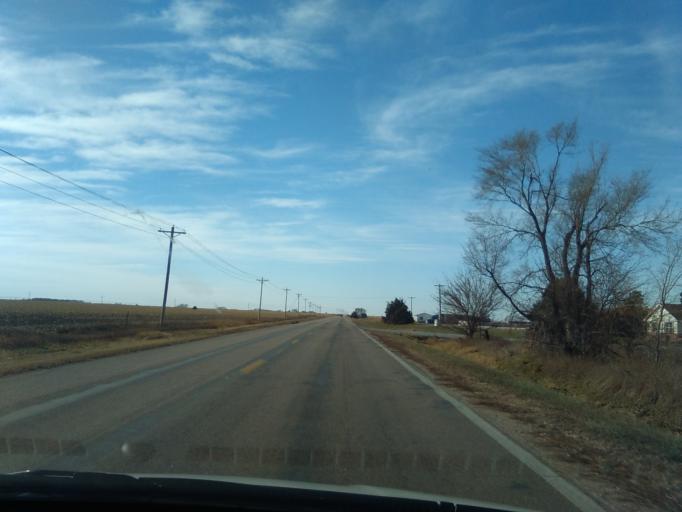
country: US
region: Nebraska
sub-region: Clay County
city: Harvard
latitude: 40.6115
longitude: -98.0994
